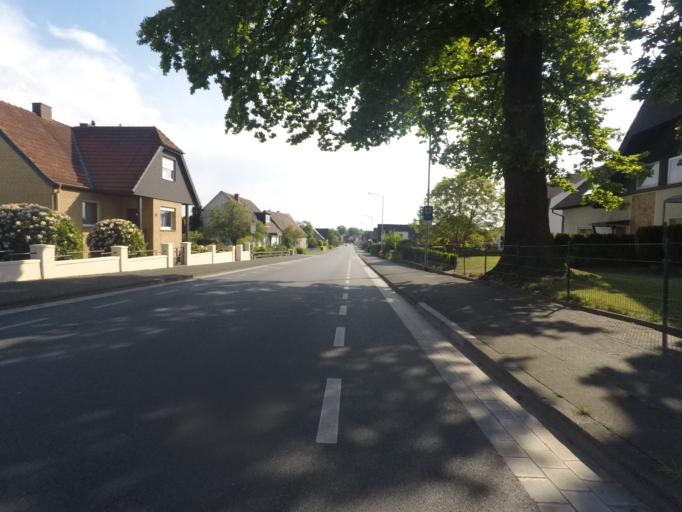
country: DE
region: North Rhine-Westphalia
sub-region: Regierungsbezirk Detmold
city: Hiddenhausen
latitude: 52.1697
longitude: 8.6362
